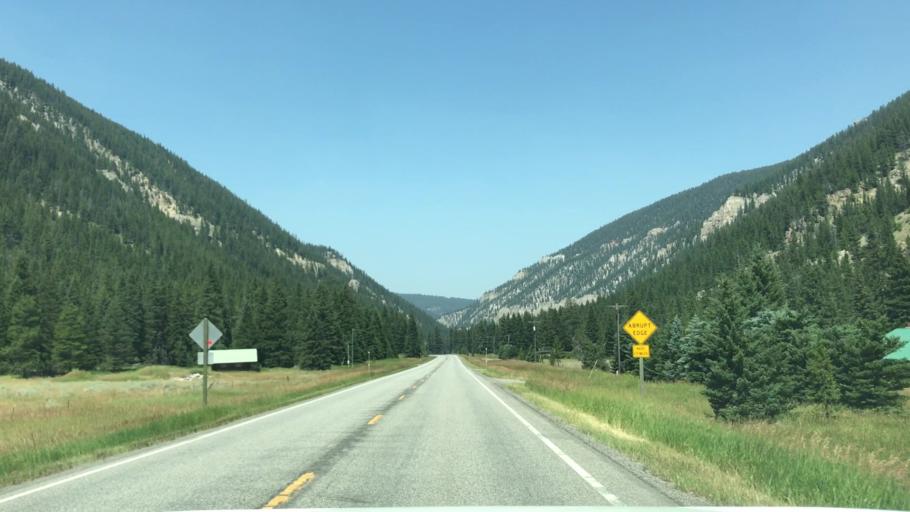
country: US
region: Montana
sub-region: Gallatin County
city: Big Sky
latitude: 45.1215
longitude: -111.2285
